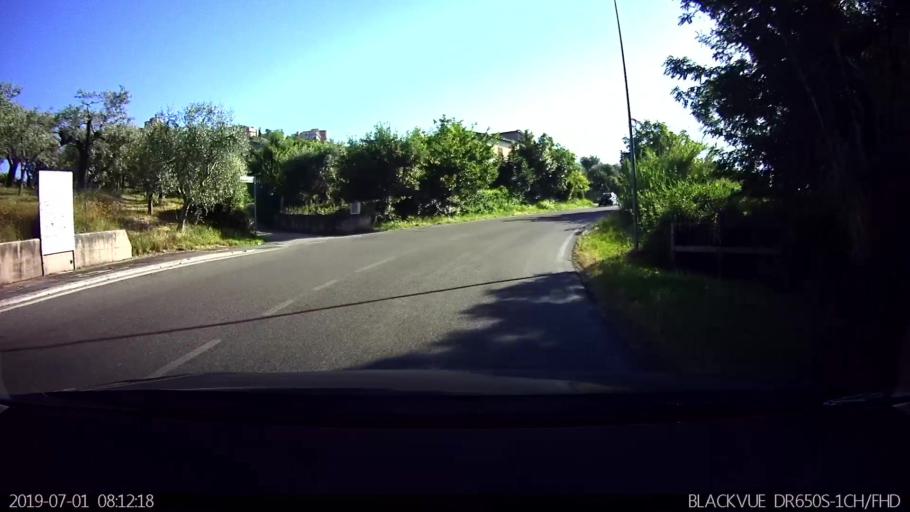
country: IT
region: Latium
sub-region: Provincia di Frosinone
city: Veroli
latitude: 41.6835
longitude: 13.4177
